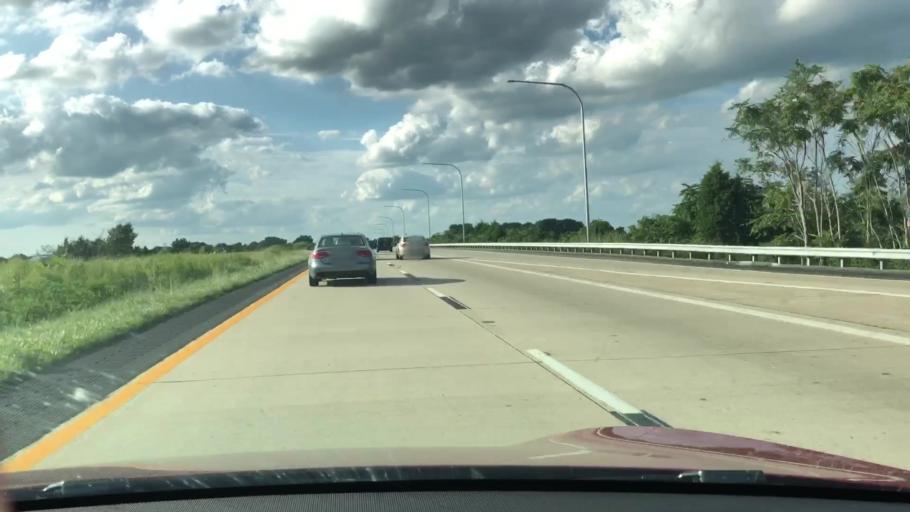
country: US
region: Delaware
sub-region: Kent County
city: Smyrna
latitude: 39.2814
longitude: -75.5884
